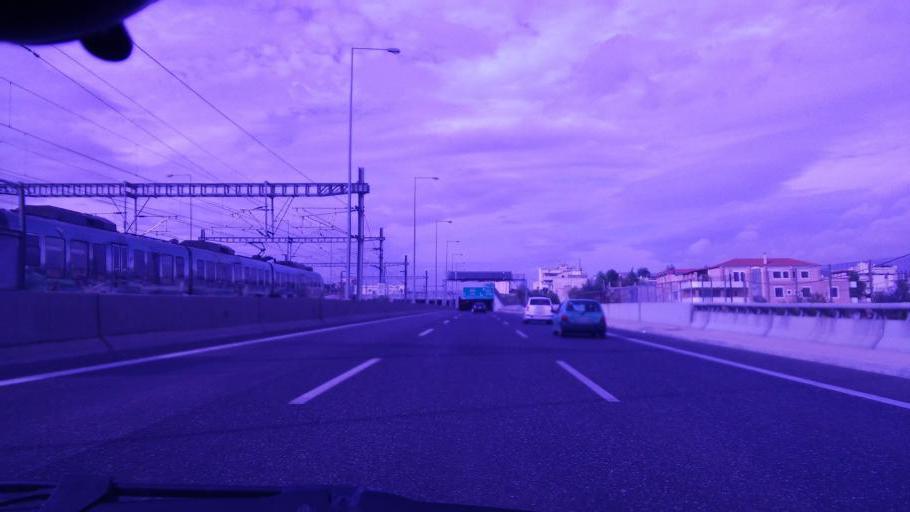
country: GR
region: Attica
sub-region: Nomarchia Dytikis Attikis
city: Zefyri
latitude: 38.0690
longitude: 23.7230
